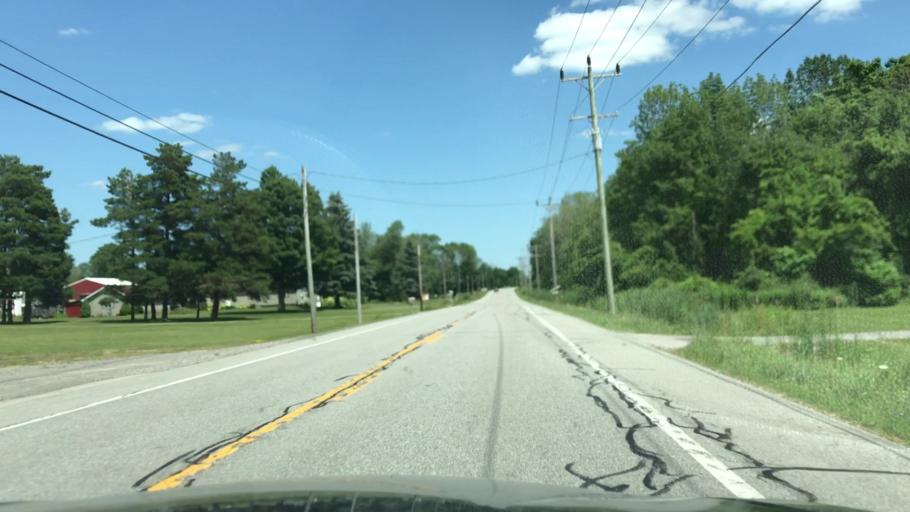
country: US
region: New York
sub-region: Wyoming County
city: Warsaw
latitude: 42.7439
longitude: -78.0715
